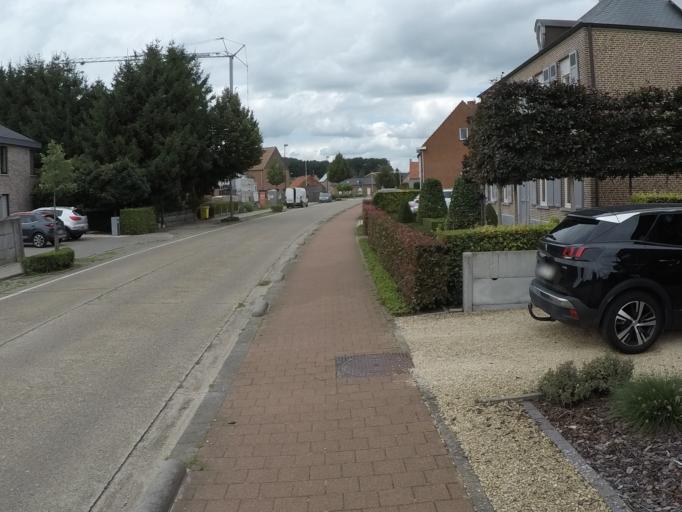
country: BE
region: Flanders
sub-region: Provincie Antwerpen
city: Vorselaar
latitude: 51.2035
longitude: 4.7648
